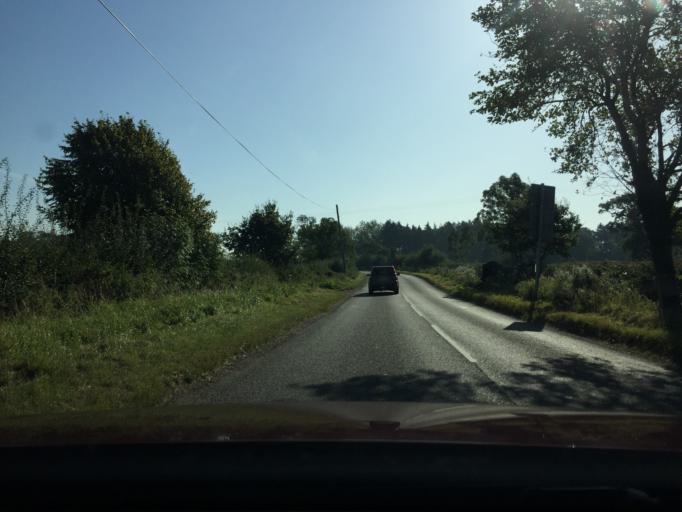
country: GB
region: England
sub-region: Leicestershire
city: Syston
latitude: 52.6790
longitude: -1.0540
